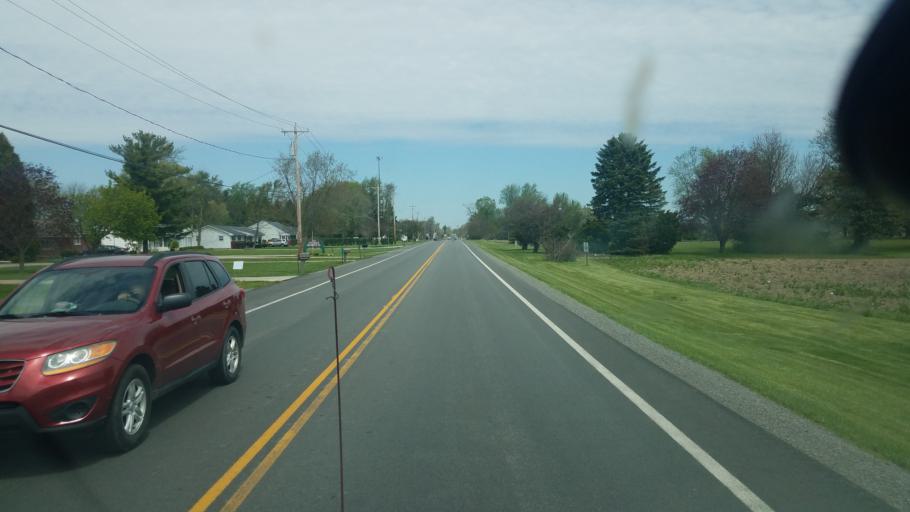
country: US
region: Ohio
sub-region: Hardin County
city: Ada
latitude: 40.7502
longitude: -83.8232
